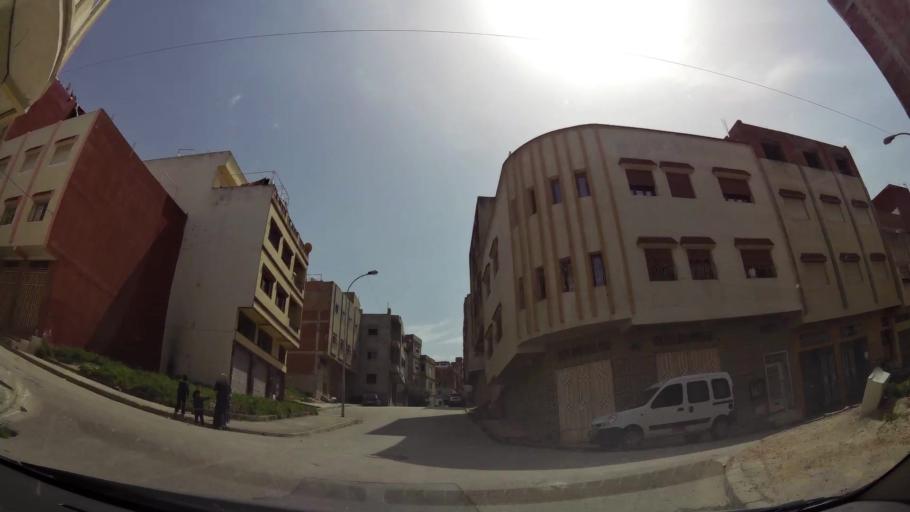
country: MA
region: Tanger-Tetouan
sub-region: Tanger-Assilah
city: Tangier
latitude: 35.7486
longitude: -5.8303
